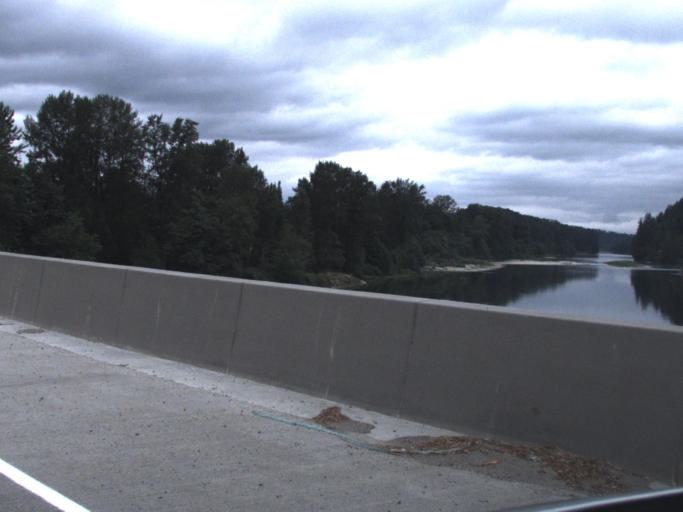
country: US
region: Washington
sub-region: Snohomish County
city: Cathcart
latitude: 47.8314
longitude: -122.0480
